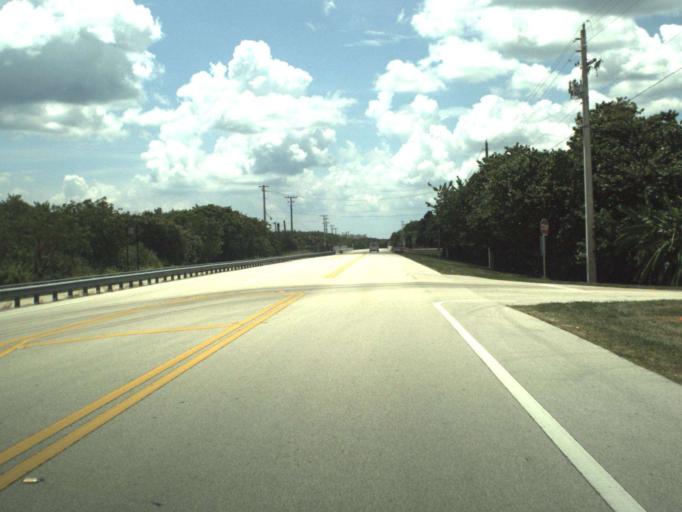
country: US
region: Florida
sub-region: Saint Lucie County
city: Hutchinson Island South
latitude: 27.3462
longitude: -80.2412
